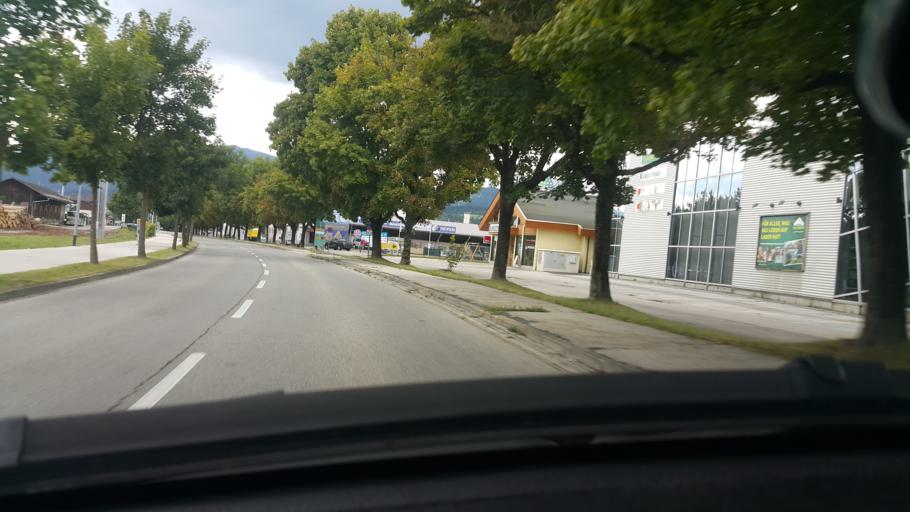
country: AT
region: Carinthia
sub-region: Politischer Bezirk Feldkirchen
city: Feldkirchen in Karnten
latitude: 46.7222
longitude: 14.1027
